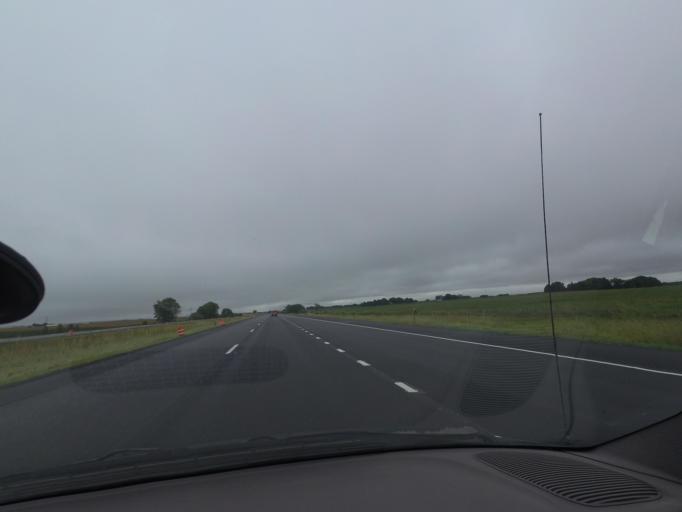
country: US
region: Illinois
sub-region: Macon County
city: Harristown
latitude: 39.8332
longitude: -89.1509
